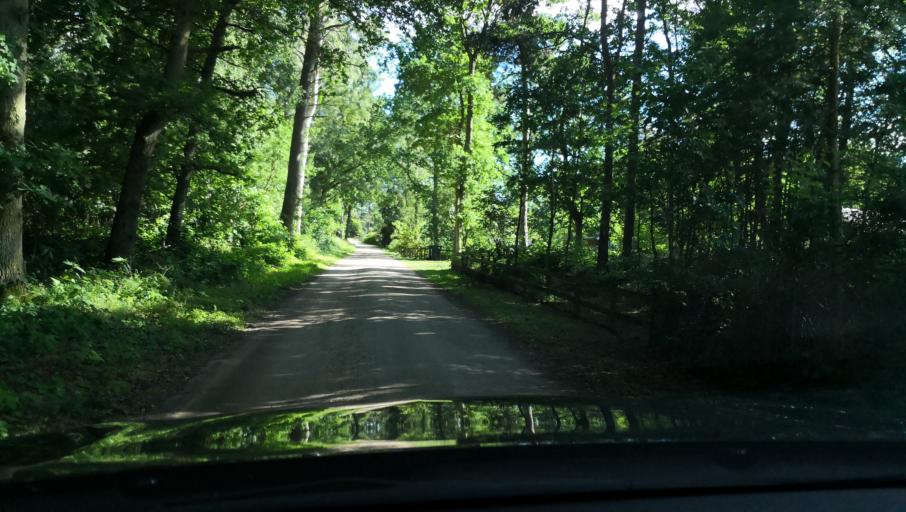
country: SE
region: Skane
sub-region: Kristianstads Kommun
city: Degeberga
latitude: 55.7934
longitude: 14.1952
